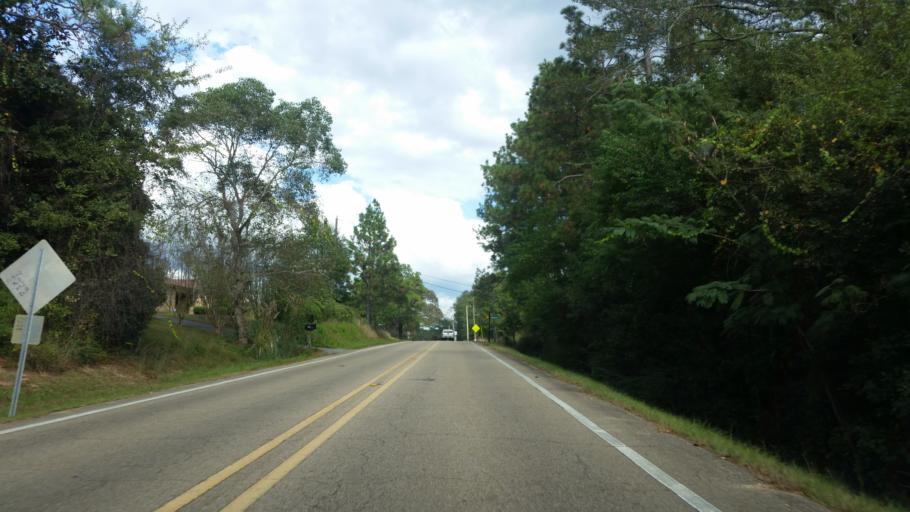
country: US
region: Mississippi
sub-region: Stone County
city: Wiggins
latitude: 30.8640
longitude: -89.1280
